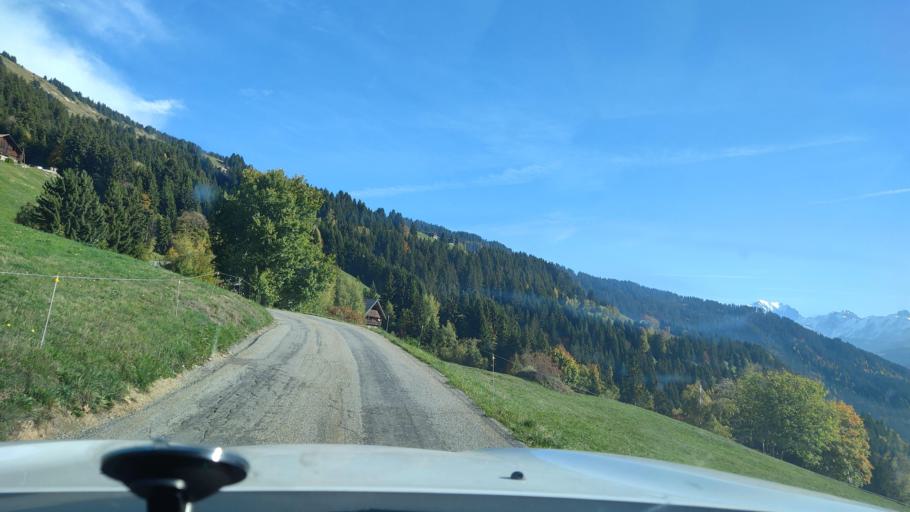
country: FR
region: Rhone-Alpes
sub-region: Departement de la Savoie
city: Beaufort
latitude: 45.7316
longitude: 6.5059
